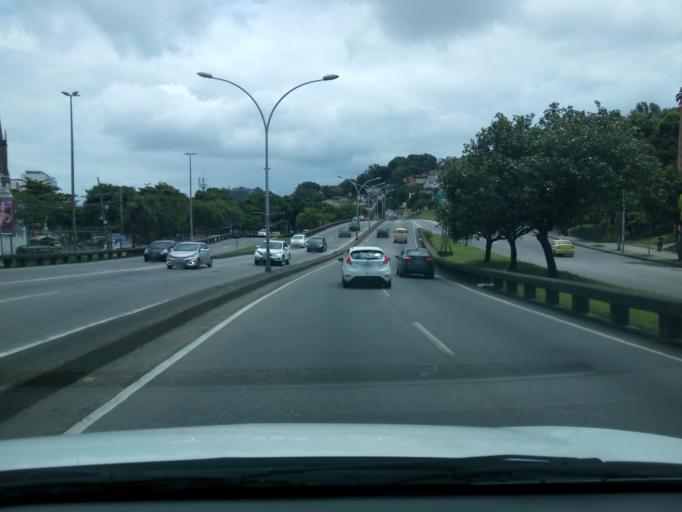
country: BR
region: Rio de Janeiro
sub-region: Rio De Janeiro
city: Rio de Janeiro
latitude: -22.9186
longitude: -43.1945
